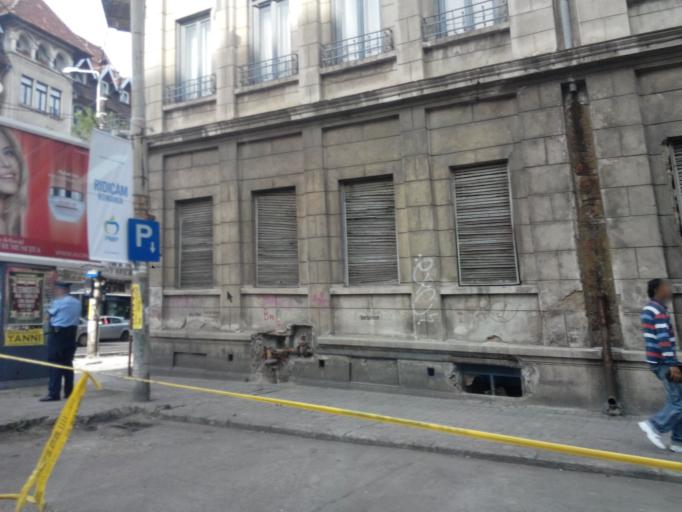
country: RO
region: Bucuresti
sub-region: Municipiul Bucuresti
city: Bucuresti
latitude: 44.4342
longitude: 26.0844
